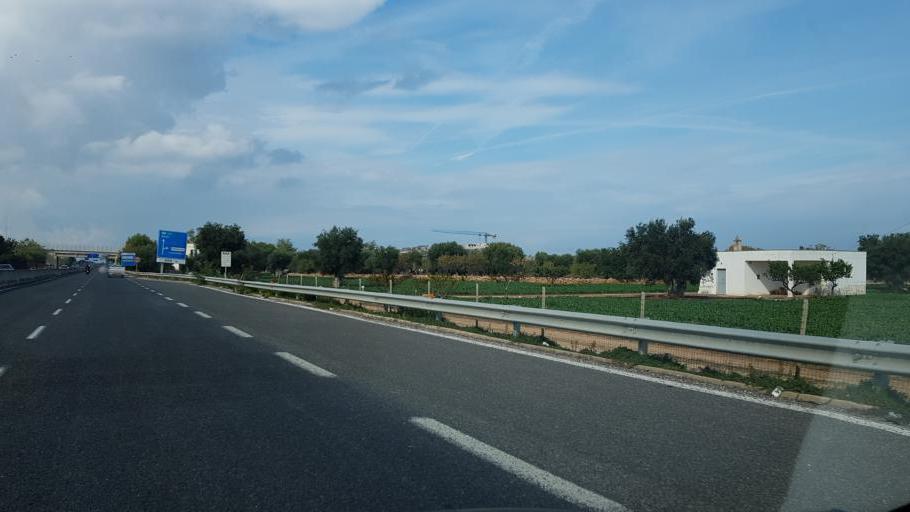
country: IT
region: Apulia
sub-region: Provincia di Bari
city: Monopoli
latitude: 40.9341
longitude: 17.2954
